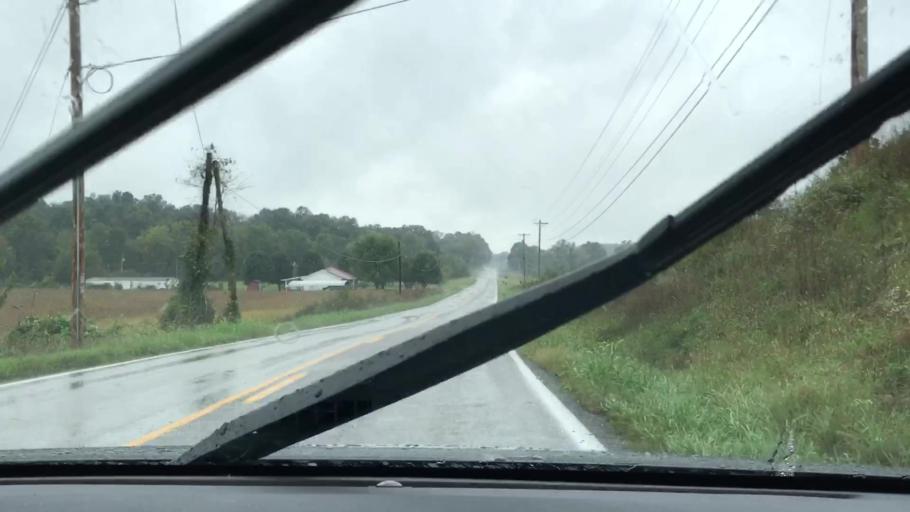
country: US
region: Kentucky
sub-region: Monroe County
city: Tompkinsville
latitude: 36.6737
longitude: -85.7216
